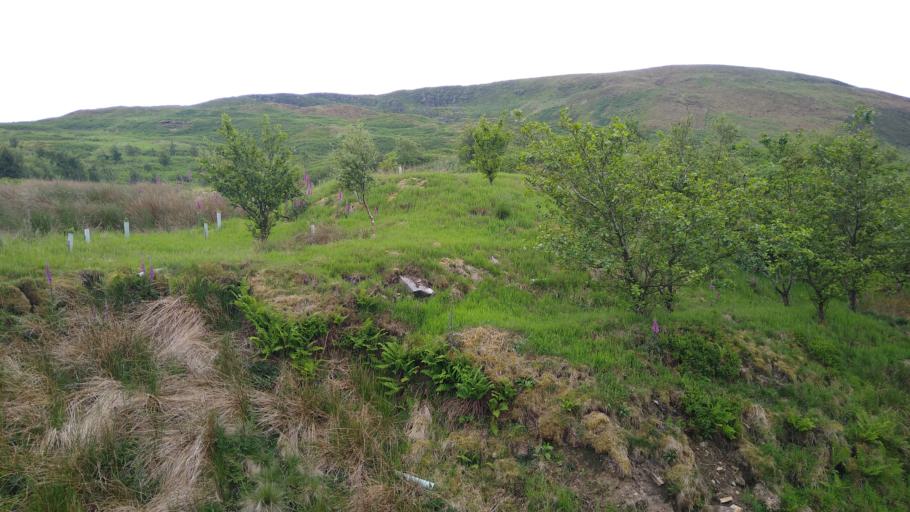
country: GB
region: England
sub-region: Cumbria
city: Brampton
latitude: 54.9073
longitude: -2.6429
